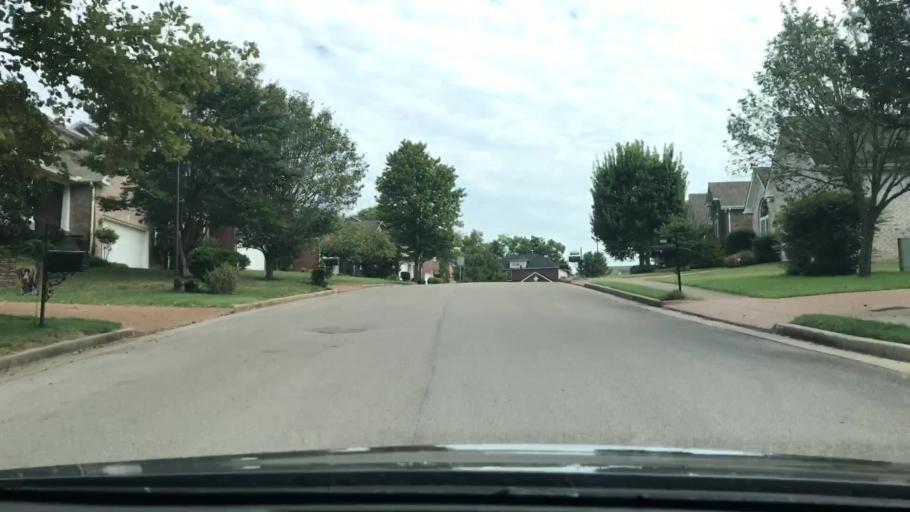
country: US
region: Tennessee
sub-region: Williamson County
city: Nolensville
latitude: 36.0052
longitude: -86.6949
